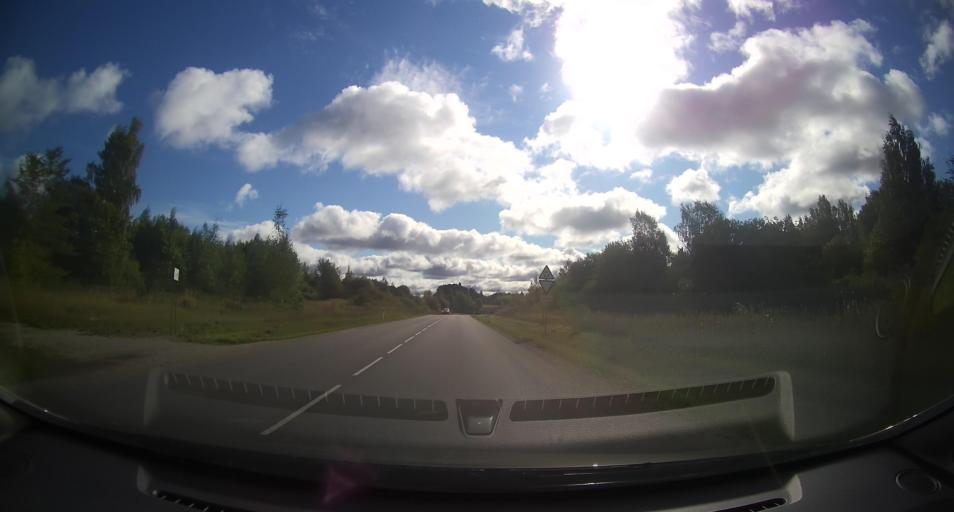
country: EE
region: Harju
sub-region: Maardu linn
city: Maardu
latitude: 59.4541
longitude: 25.0255
